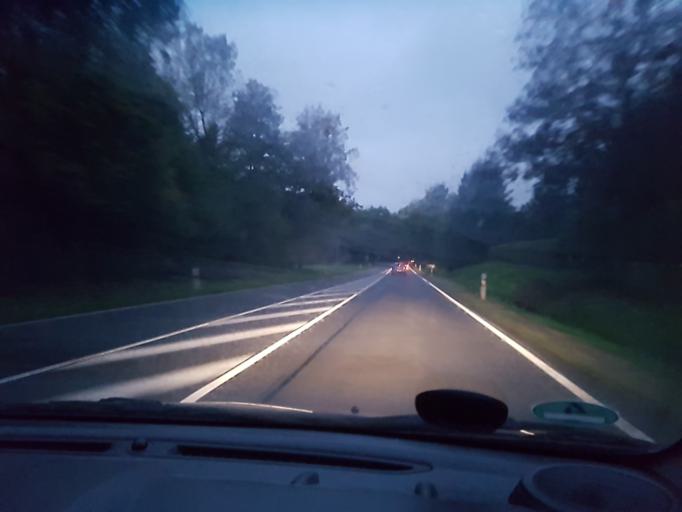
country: DE
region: Lower Saxony
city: Delligsen
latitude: 51.9394
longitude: 9.8210
